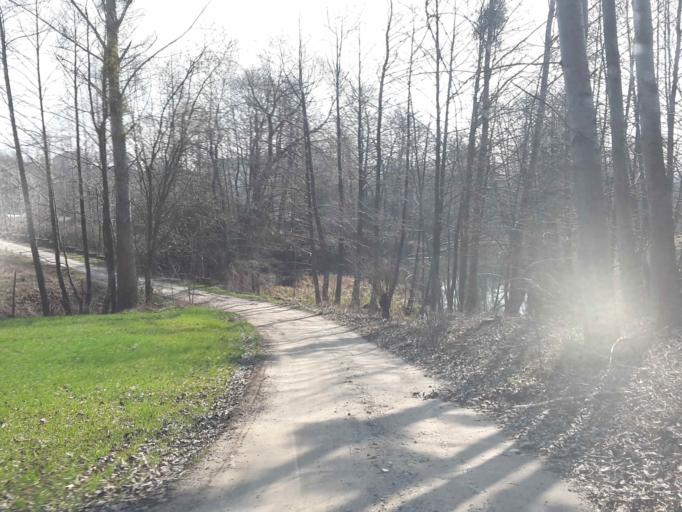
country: PL
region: Kujawsko-Pomorskie
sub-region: Powiat brodnicki
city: Brodnica
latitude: 53.3224
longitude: 19.3682
